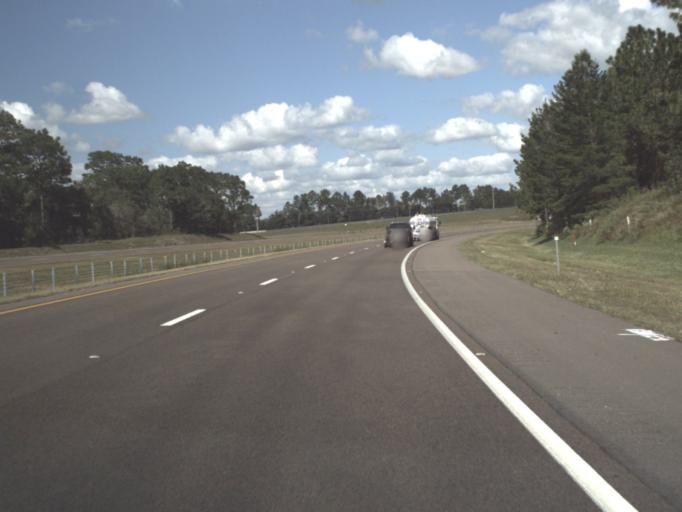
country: US
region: Florida
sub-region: Hernando County
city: Spring Hill
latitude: 28.4878
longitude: -82.4837
